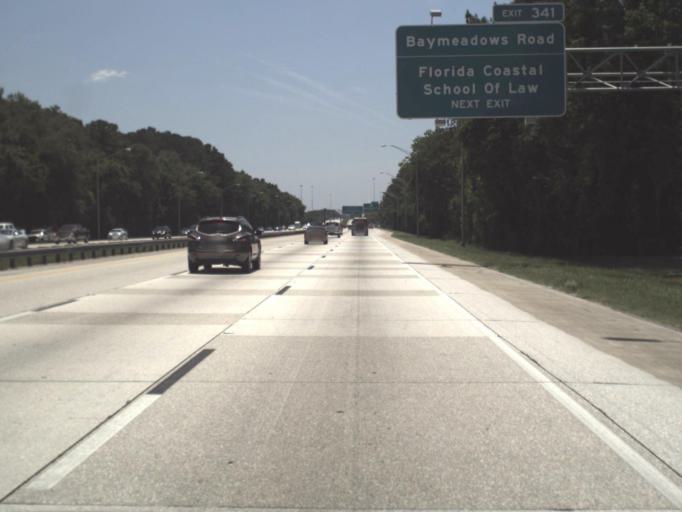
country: US
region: Florida
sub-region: Duval County
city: Jacksonville
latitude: 30.2300
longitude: -81.5774
